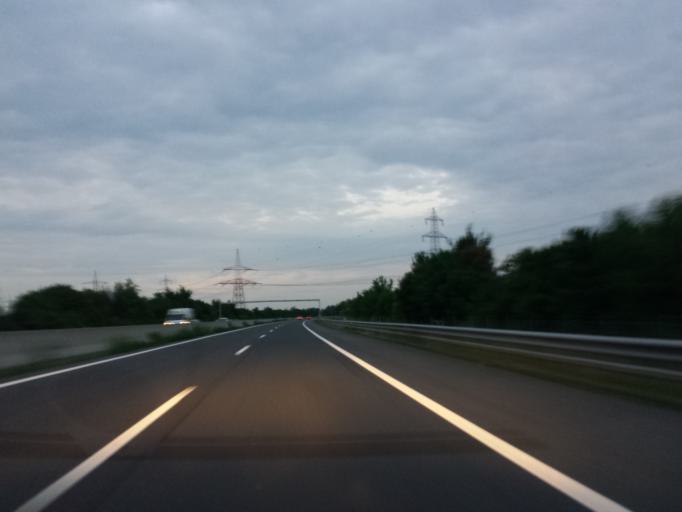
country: AT
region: Lower Austria
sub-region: Politischer Bezirk Baden
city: Trumau
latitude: 47.9772
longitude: 16.3722
